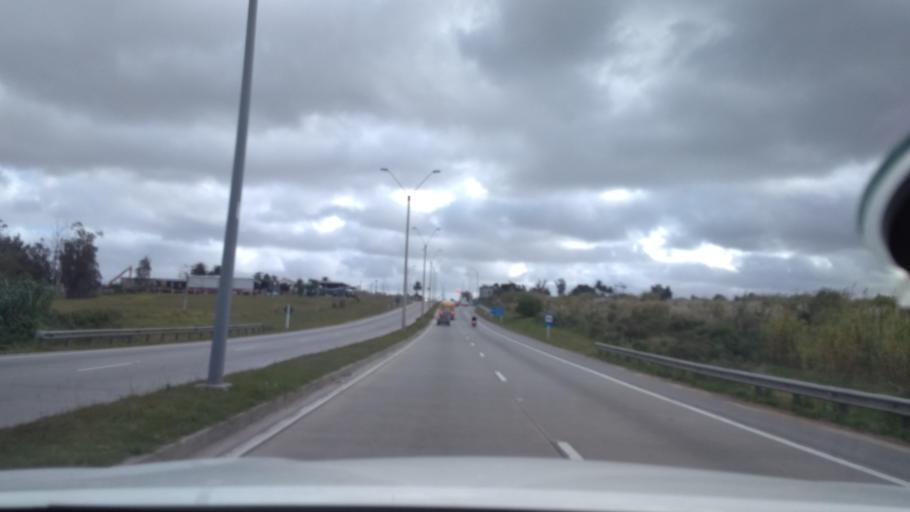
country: UY
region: Canelones
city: Toledo
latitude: -34.7949
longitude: -56.1196
